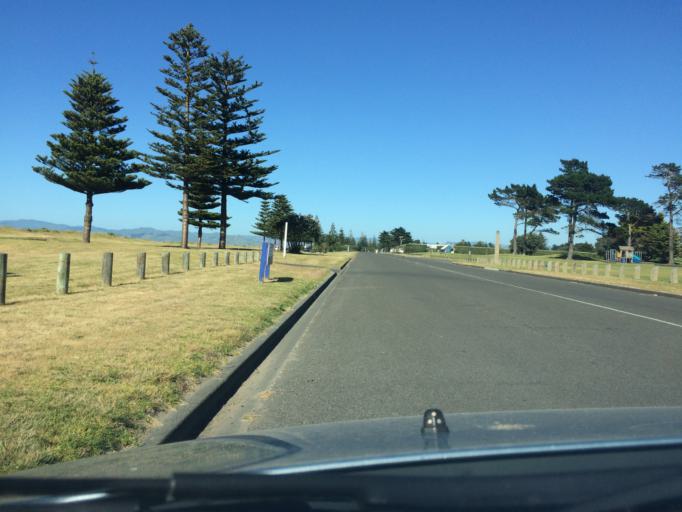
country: NZ
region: Gisborne
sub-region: Gisborne District
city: Gisborne
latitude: -38.6703
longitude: 178.0038
